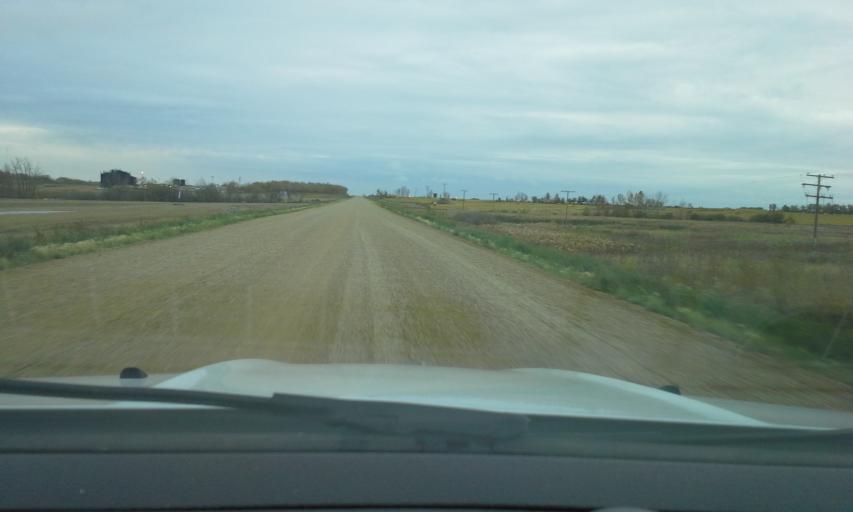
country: CA
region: Saskatchewan
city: Lloydminster
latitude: 53.2789
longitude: -109.8084
